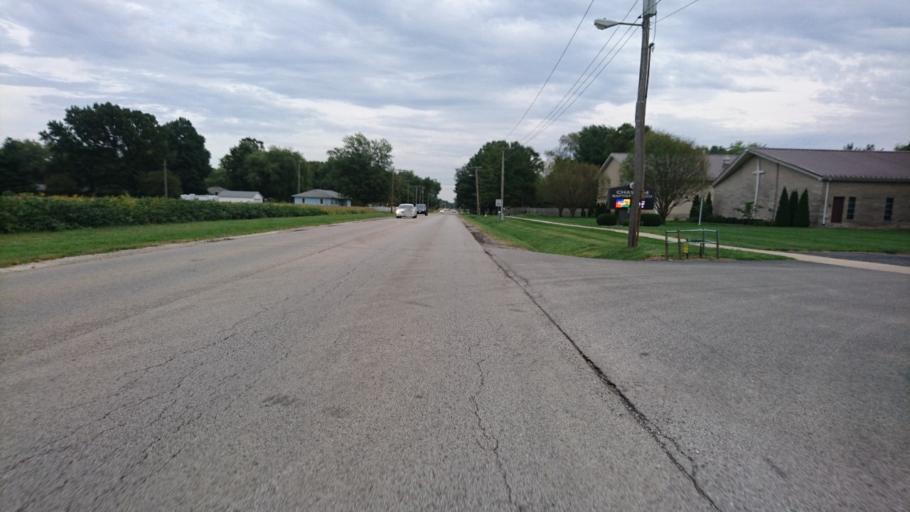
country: US
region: Illinois
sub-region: Sangamon County
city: Chatham
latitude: 39.6768
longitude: -89.6877
